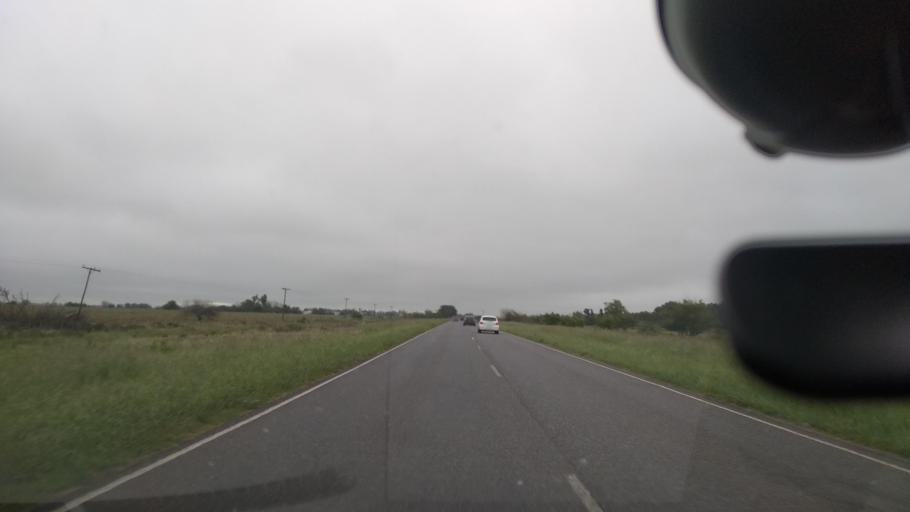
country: AR
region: Buenos Aires
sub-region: Partido de Magdalena
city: Magdalena
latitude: -35.2398
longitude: -57.6913
